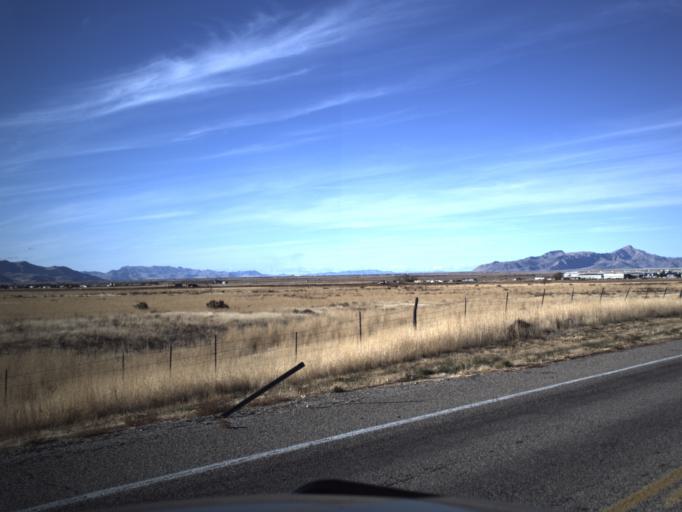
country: US
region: Utah
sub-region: Tooele County
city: Erda
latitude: 40.5897
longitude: -112.3703
